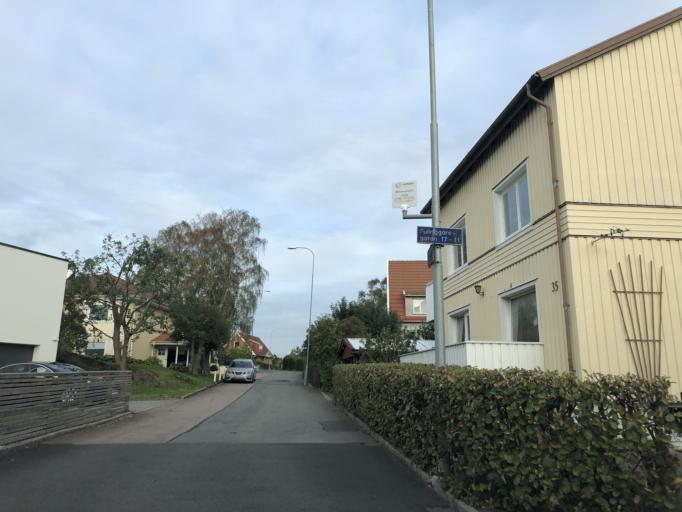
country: SE
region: Vaestra Goetaland
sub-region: Goteborg
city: Majorna
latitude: 57.6750
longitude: 11.8738
